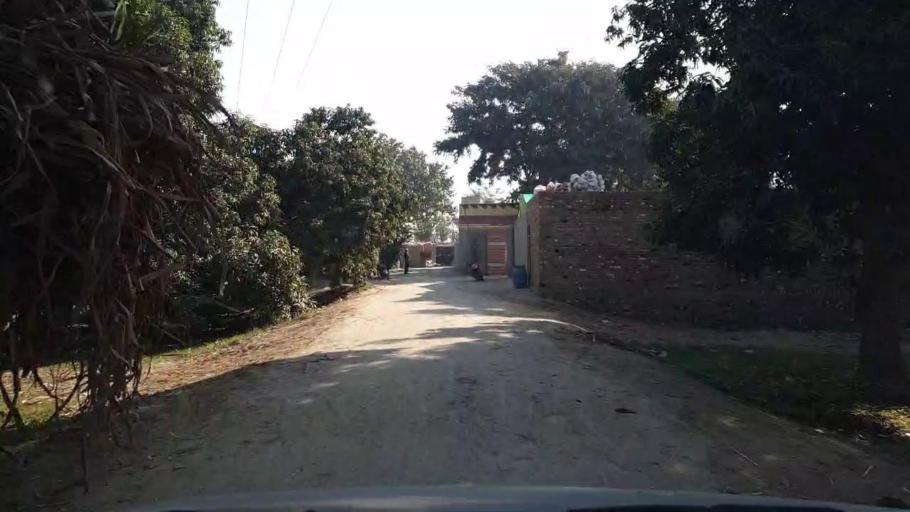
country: PK
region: Sindh
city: Tando Jam
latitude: 25.4261
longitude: 68.6110
